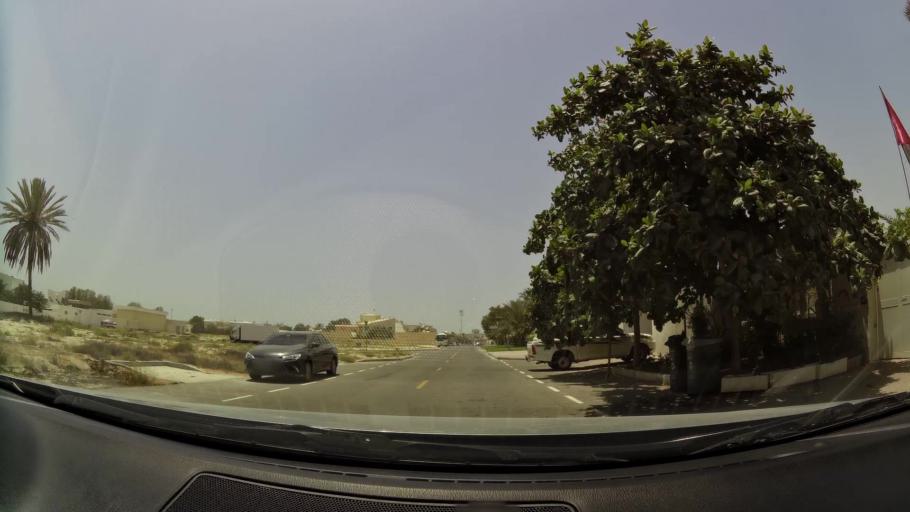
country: AE
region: Dubai
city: Dubai
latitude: 25.1723
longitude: 55.2221
